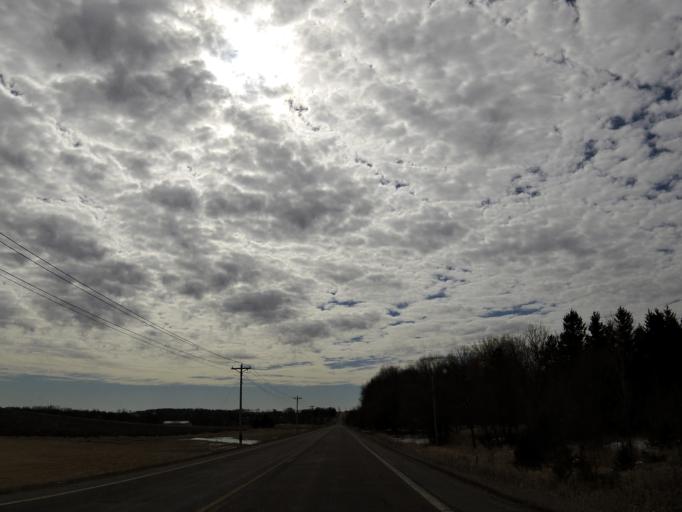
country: US
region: Minnesota
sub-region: Scott County
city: Jordan
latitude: 44.6510
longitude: -93.5626
